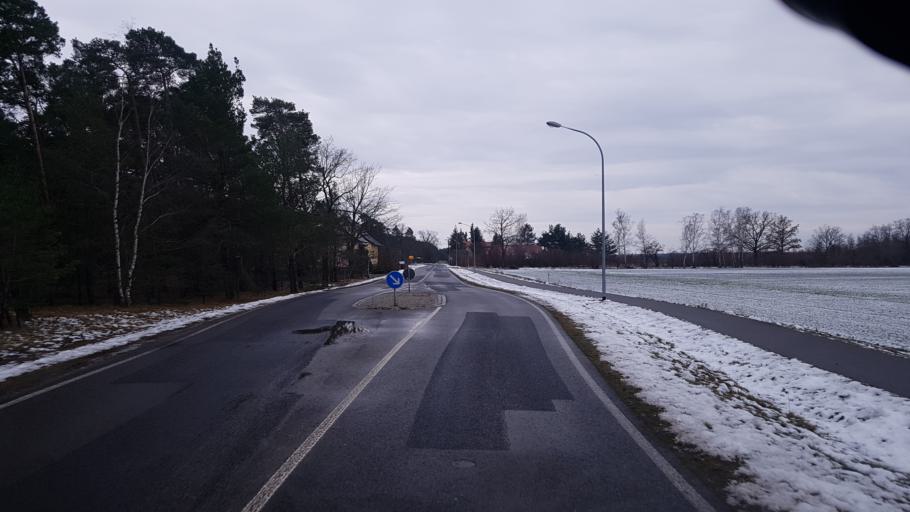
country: DE
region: Brandenburg
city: Janschwalde
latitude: 51.8569
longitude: 14.5053
